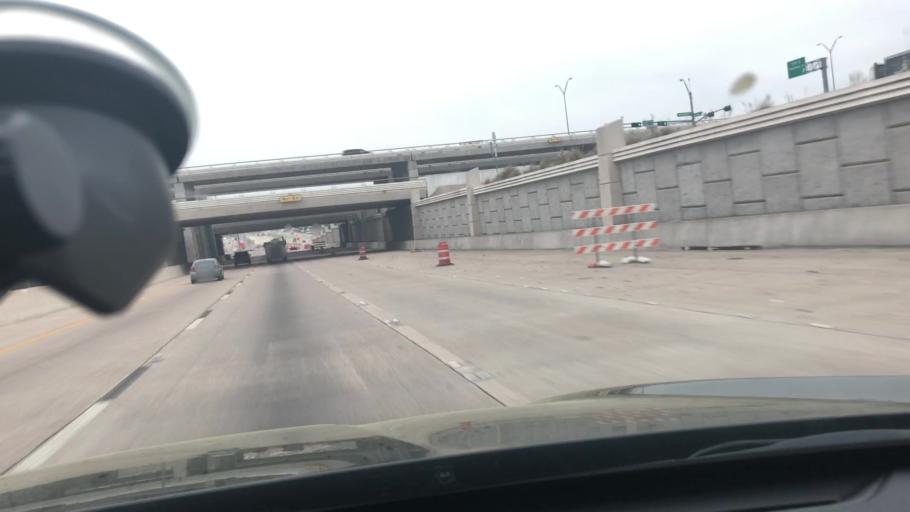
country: US
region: Texas
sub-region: Bell County
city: Temple
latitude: 31.0900
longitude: -97.3886
